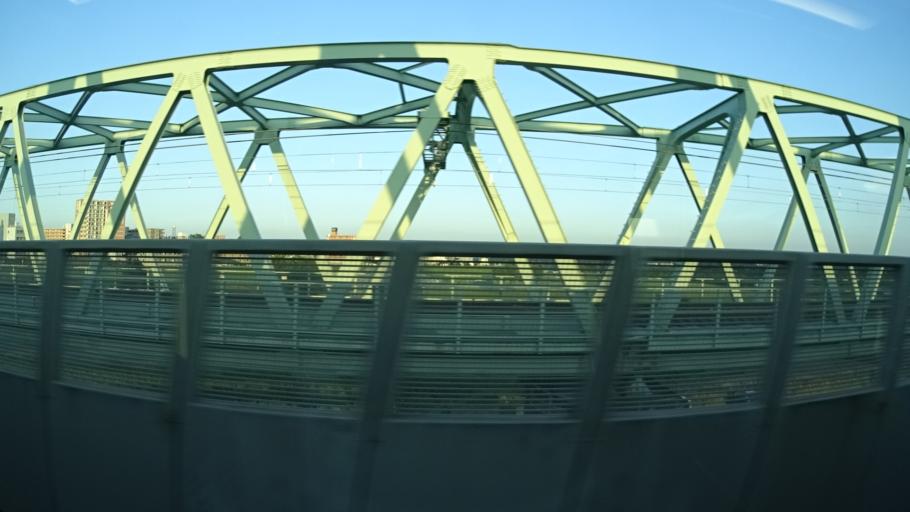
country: JP
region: Ibaraki
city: Toride
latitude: 35.8918
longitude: 140.0604
